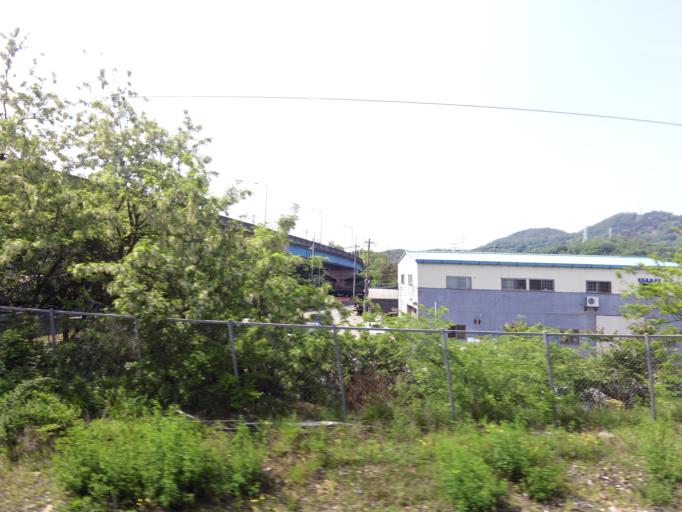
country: KR
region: Daegu
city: Daegu
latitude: 35.8819
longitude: 128.5342
